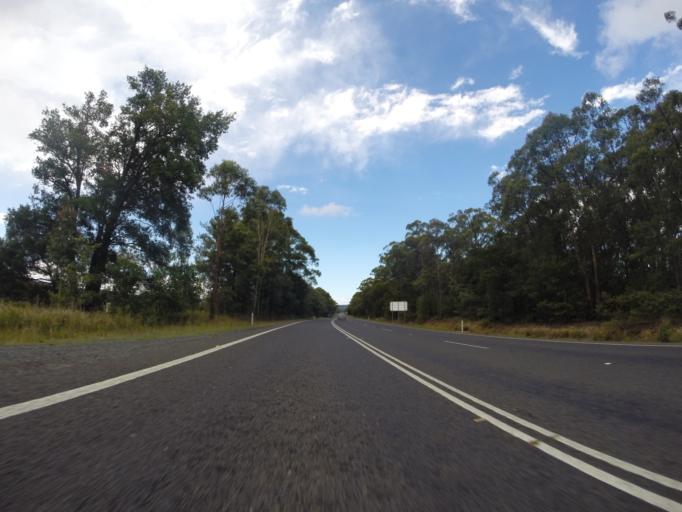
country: AU
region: New South Wales
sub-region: Shoalhaven Shire
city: Falls Creek
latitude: -35.1160
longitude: 150.4842
